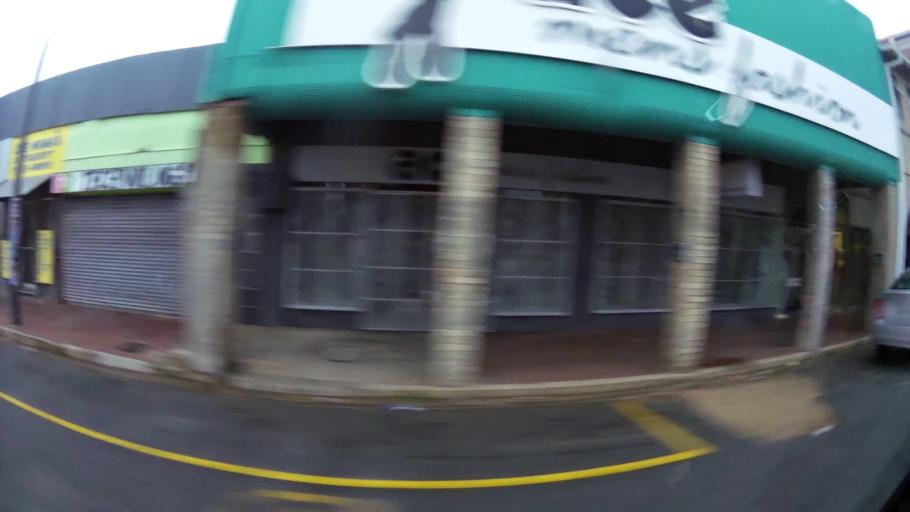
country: ZA
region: Eastern Cape
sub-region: Nelson Mandela Bay Metropolitan Municipality
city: Port Elizabeth
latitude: -33.9444
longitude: 25.6062
